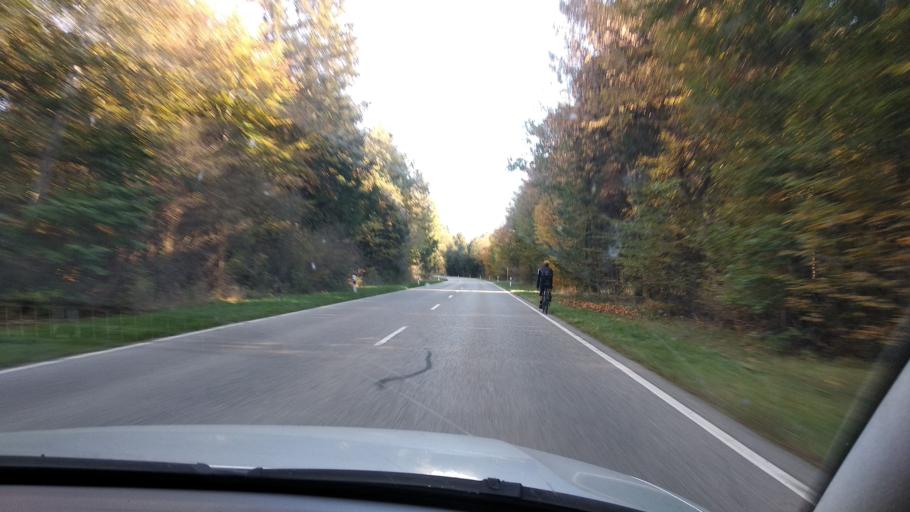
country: DE
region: Bavaria
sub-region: Upper Bavaria
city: Grasbrunn
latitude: 48.0655
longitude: 11.7378
